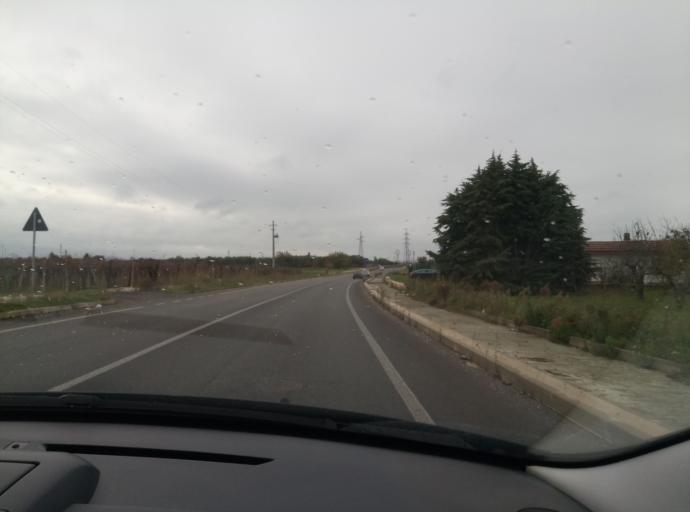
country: IT
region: Apulia
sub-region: Provincia di Bari
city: Acquaviva delle Fonti
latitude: 40.8908
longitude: 16.8297
